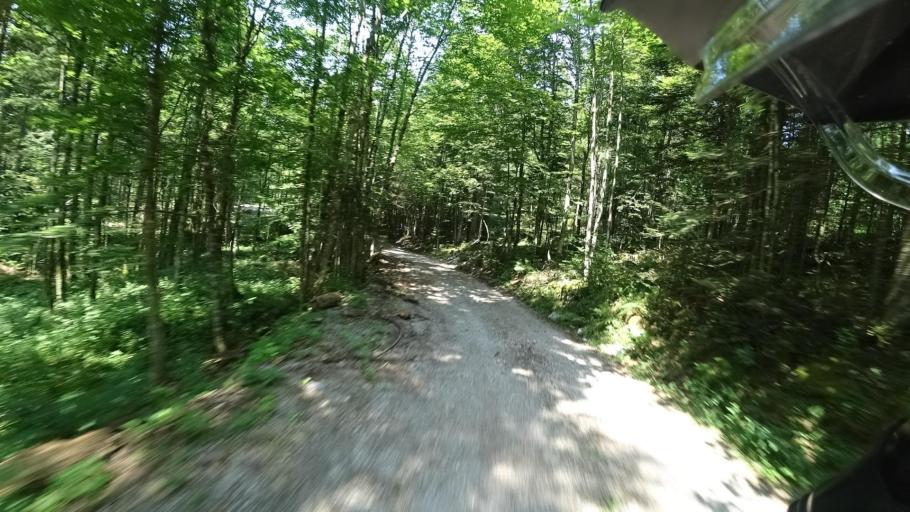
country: HR
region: Primorsko-Goranska
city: Vrbovsko
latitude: 45.3424
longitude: 15.0378
